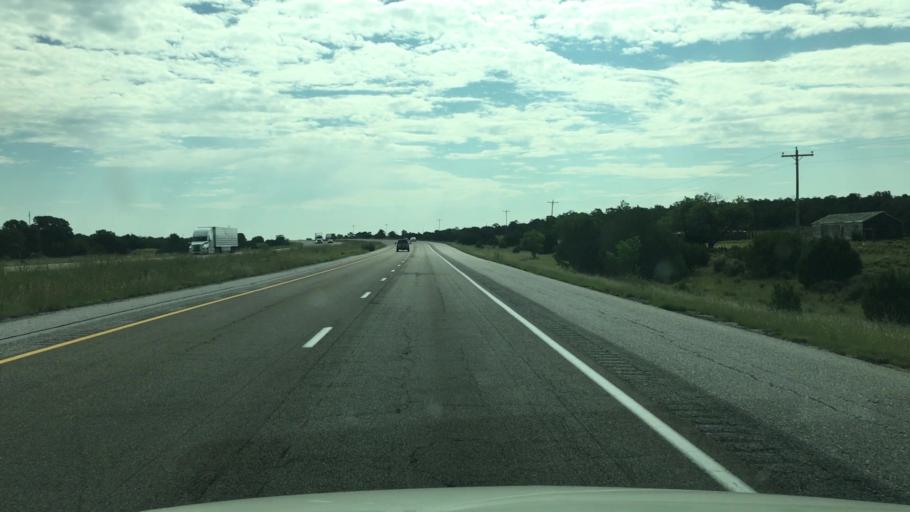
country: US
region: New Mexico
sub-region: Torrance County
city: Moriarty
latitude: 35.0019
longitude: -105.5578
